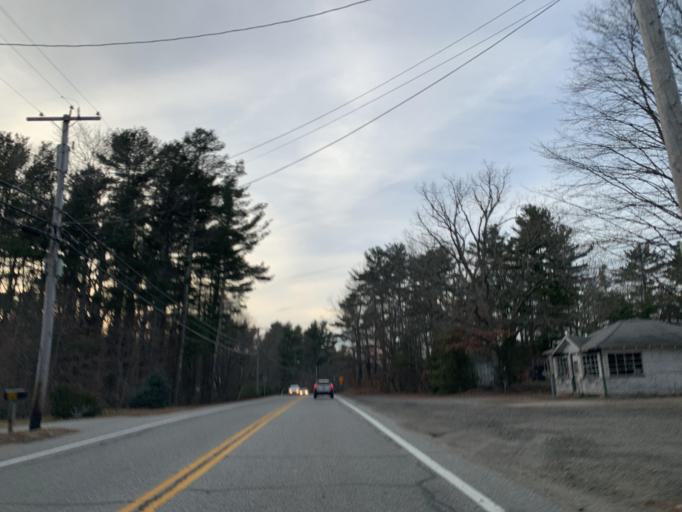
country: US
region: Rhode Island
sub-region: Providence County
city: Chepachet
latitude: 41.9055
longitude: -71.6551
